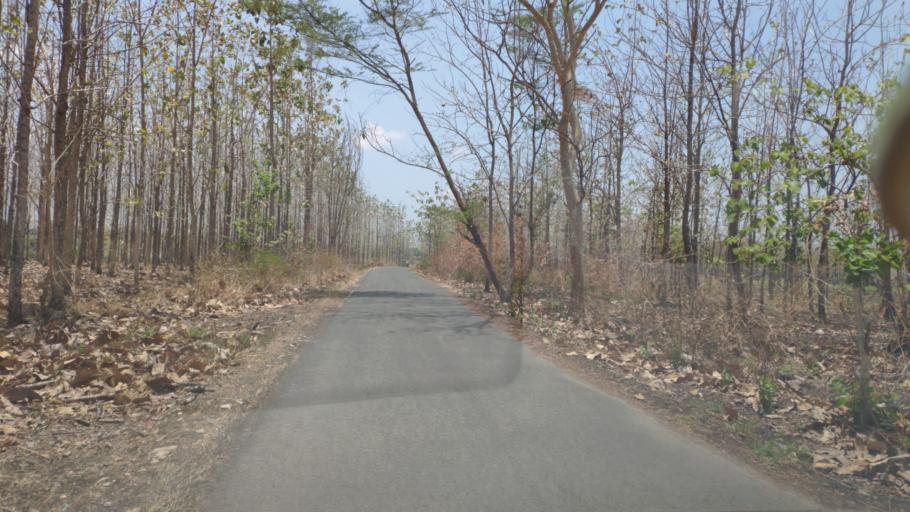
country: ID
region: Central Java
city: Mendenrejo
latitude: -7.3110
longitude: 111.3758
